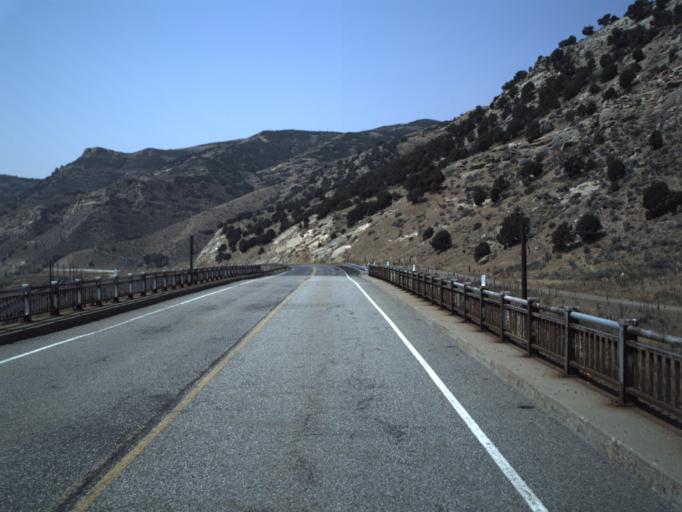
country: US
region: Utah
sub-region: Summit County
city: Coalville
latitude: 41.0678
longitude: -111.2705
